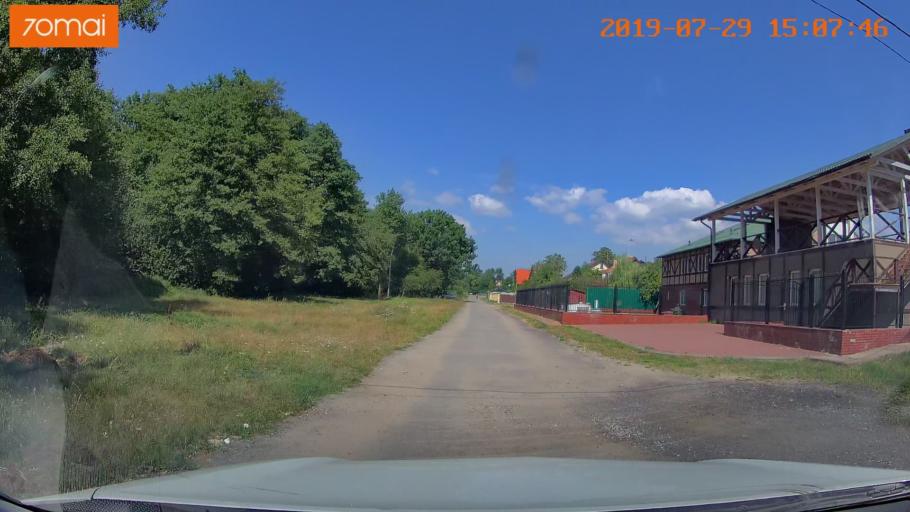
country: RU
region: Kaliningrad
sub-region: Gorod Kaliningrad
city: Baltiysk
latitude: 54.6780
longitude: 19.9146
